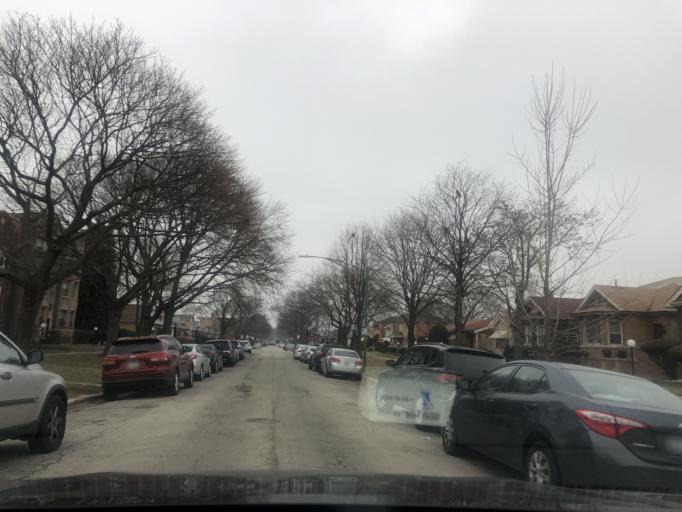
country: US
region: Illinois
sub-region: Cook County
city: Evergreen Park
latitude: 41.7482
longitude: -87.6214
